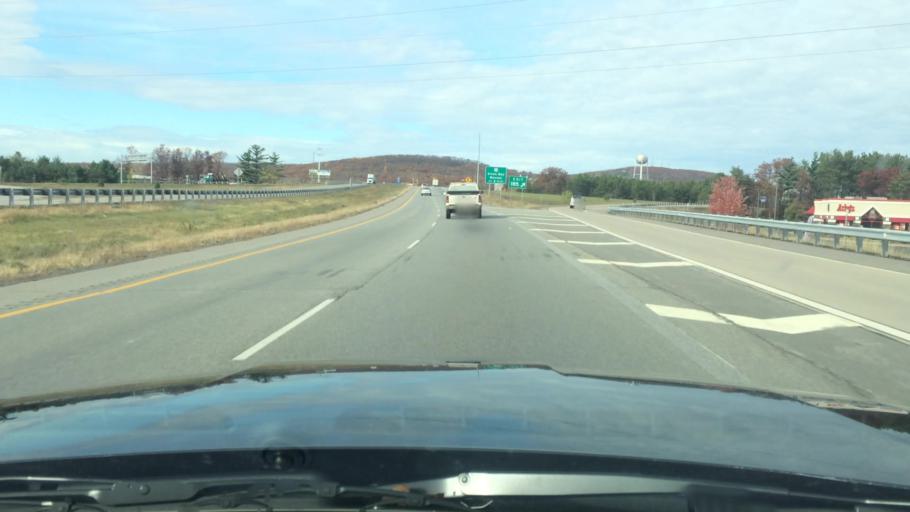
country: US
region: Wisconsin
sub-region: Marathon County
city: Evergreen
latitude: 44.8603
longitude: -89.6384
